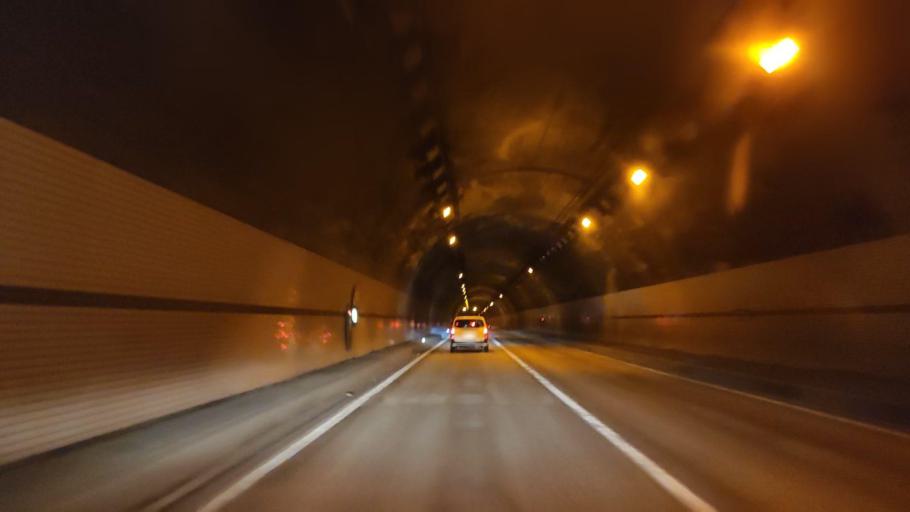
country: JP
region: Toyama
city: Yatsuomachi-higashikumisaka
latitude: 36.4976
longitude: 137.2359
